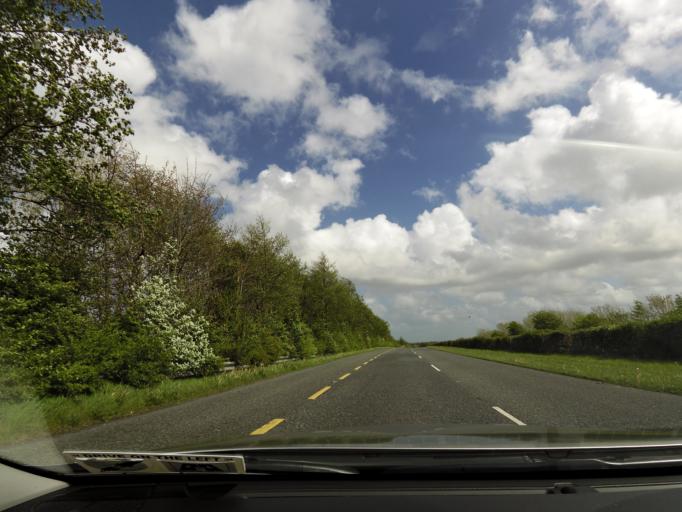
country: IE
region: Connaught
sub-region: County Galway
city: Oranmore
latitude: 53.2781
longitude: -8.9393
